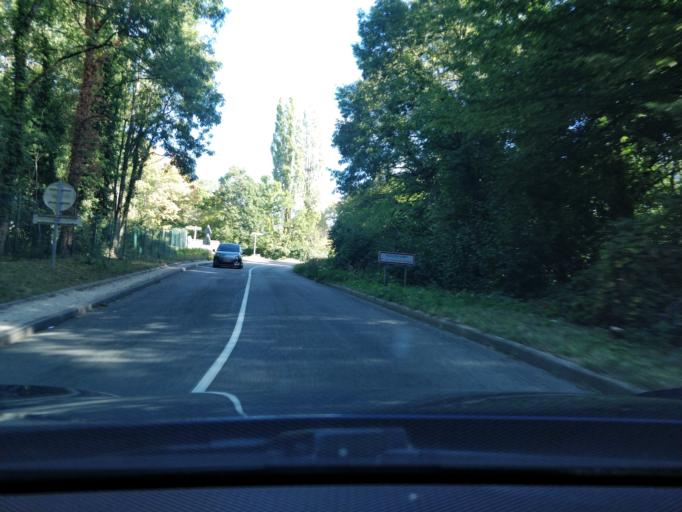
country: FR
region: Ile-de-France
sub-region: Departement de l'Essonne
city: Forges-les-Bains
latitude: 48.6470
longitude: 2.1030
